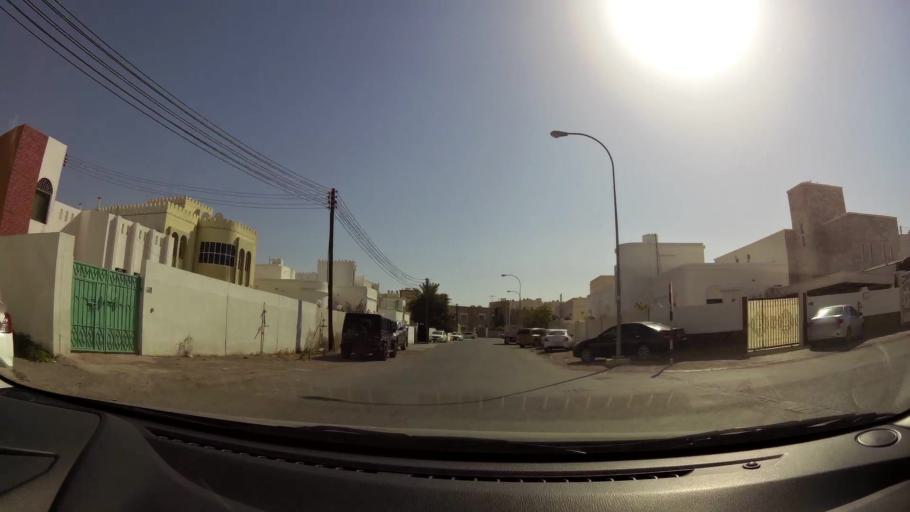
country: OM
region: Muhafazat Masqat
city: As Sib al Jadidah
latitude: 23.6278
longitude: 58.2031
